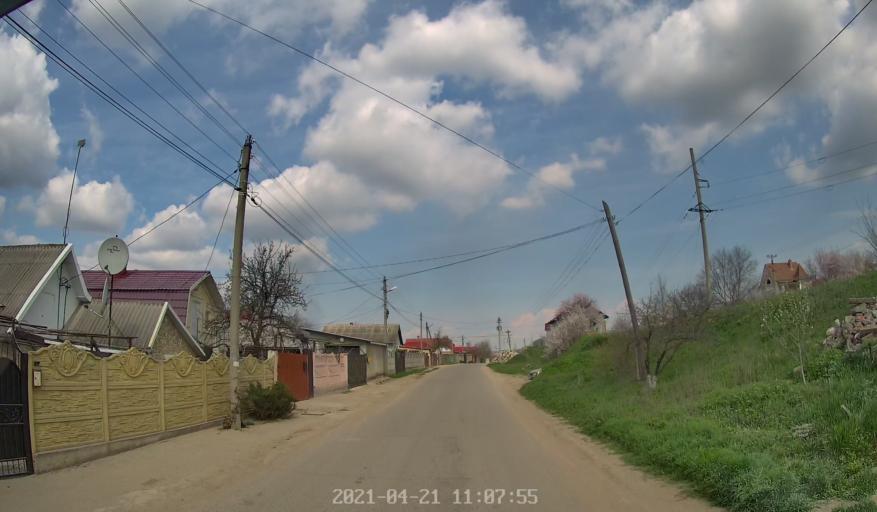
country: MD
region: Chisinau
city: Singera
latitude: 46.9513
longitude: 28.9434
